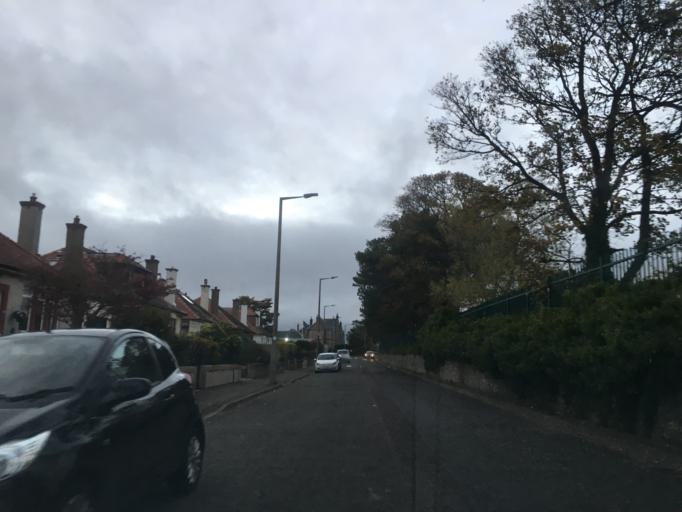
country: GB
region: Scotland
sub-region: Midlothian
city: Loanhead
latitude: 55.9074
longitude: -3.1675
